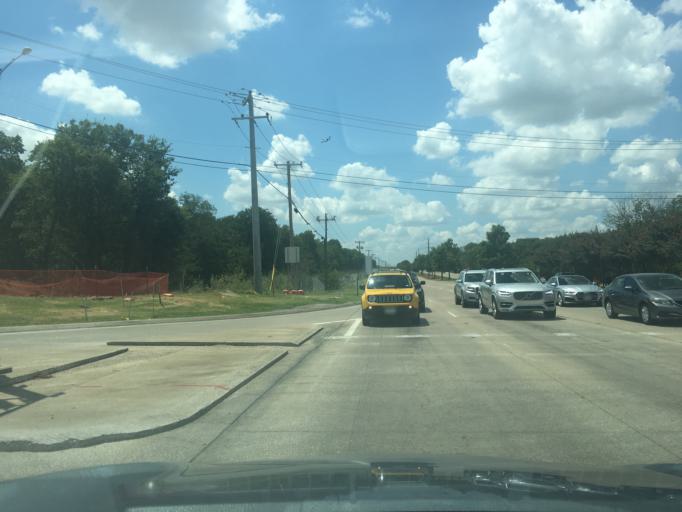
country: US
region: Texas
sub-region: Dallas County
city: Coppell
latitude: 32.9554
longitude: -97.0479
